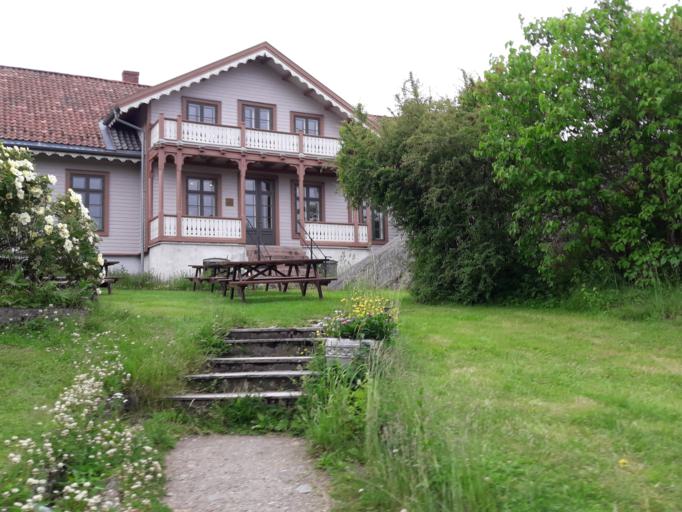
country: NO
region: Akershus
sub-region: Frogn
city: Drobak
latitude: 59.6772
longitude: 10.6065
